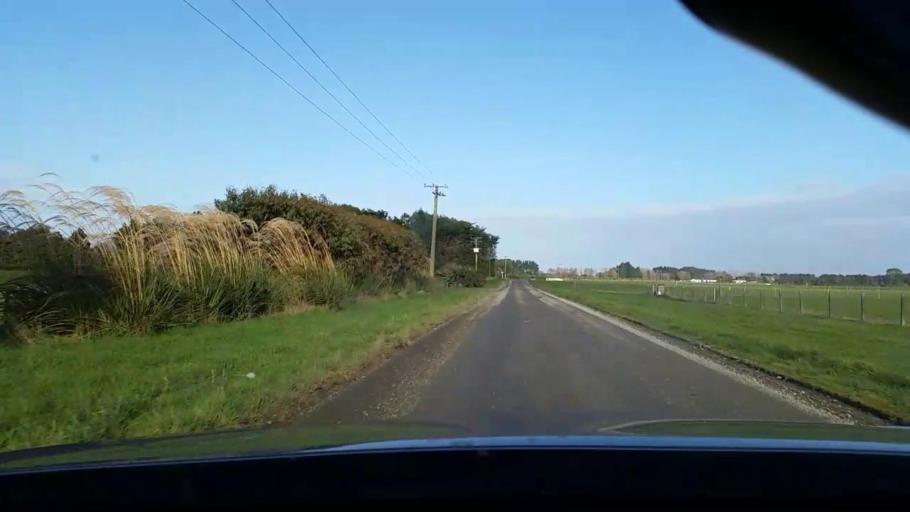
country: NZ
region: Southland
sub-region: Invercargill City
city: Invercargill
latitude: -46.3074
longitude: 168.3033
